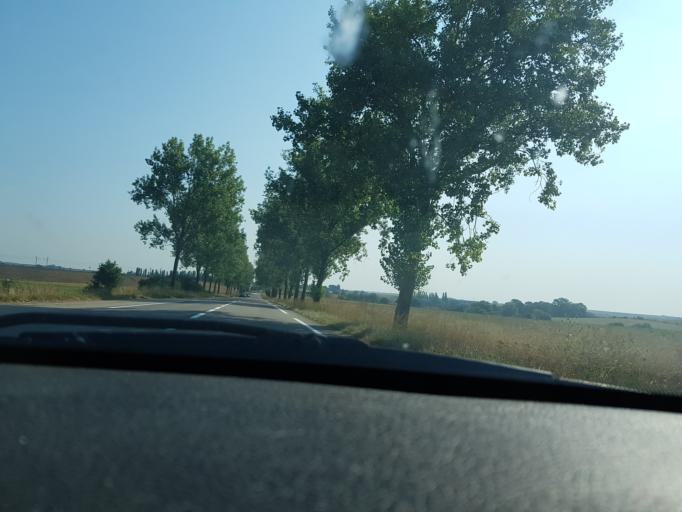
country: FR
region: Lorraine
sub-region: Departement de Meurthe-et-Moselle
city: Pont-a-Mousson
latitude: 48.9377
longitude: 6.1159
